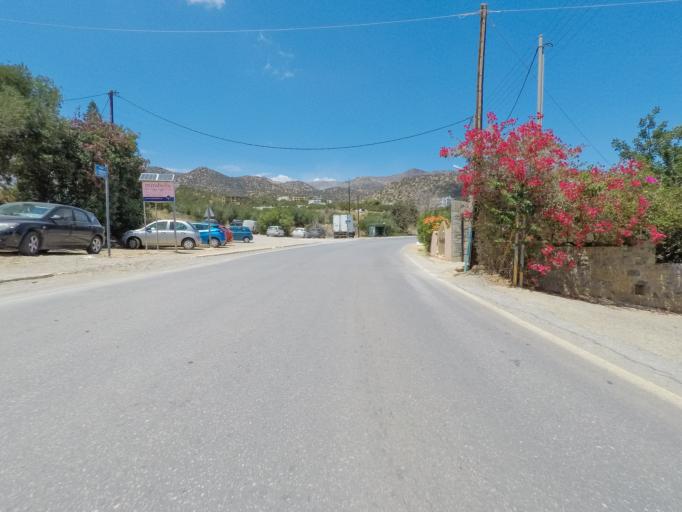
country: GR
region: Crete
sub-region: Nomos Lasithiou
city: Agios Nikolaos
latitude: 35.2140
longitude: 25.7117
